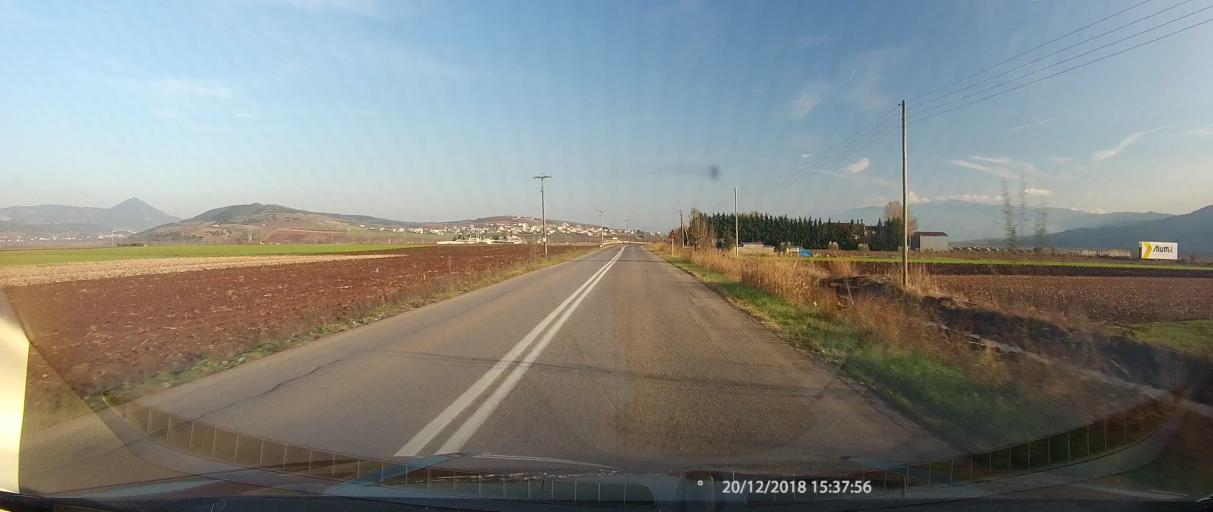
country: GR
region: Central Greece
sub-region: Nomos Fthiotidos
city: Stavros
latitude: 38.9083
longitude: 22.3400
